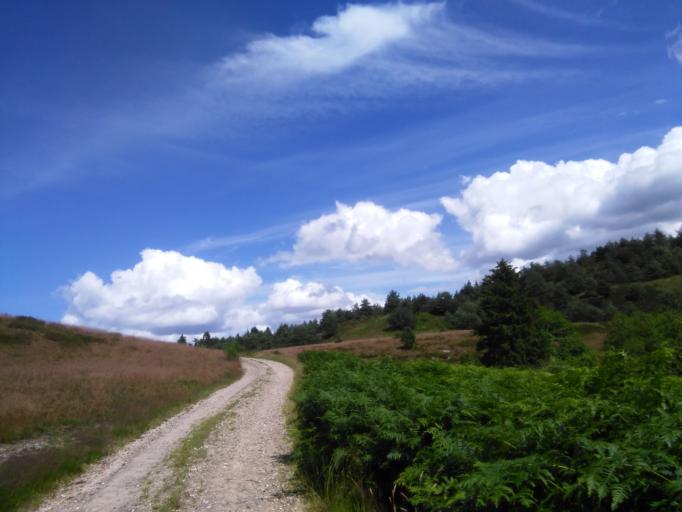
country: DK
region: Central Jutland
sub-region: Silkeborg Kommune
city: Virklund
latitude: 56.0717
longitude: 9.4516
